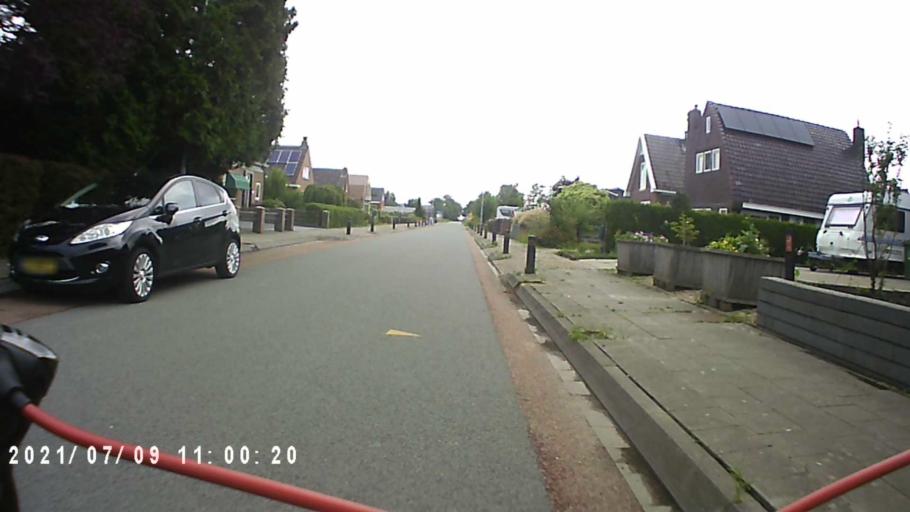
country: NL
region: Groningen
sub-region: Gemeente Bedum
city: Bedum
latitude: 53.2730
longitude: 6.7034
